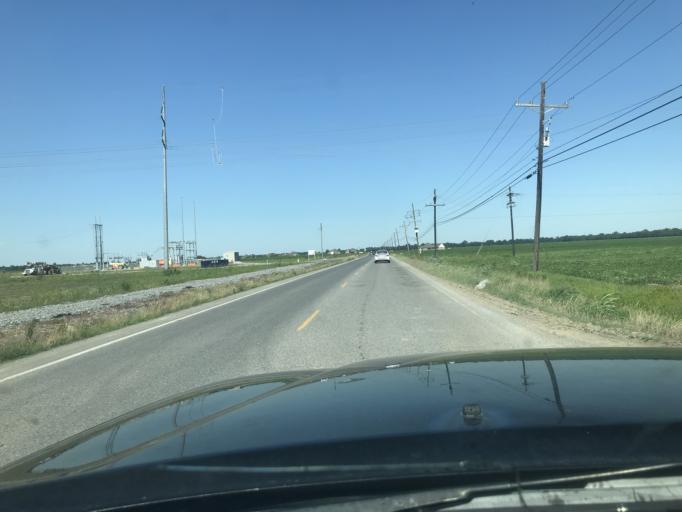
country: US
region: Louisiana
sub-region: West Baton Rouge Parish
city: Brusly
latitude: 30.4687
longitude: -91.3142
